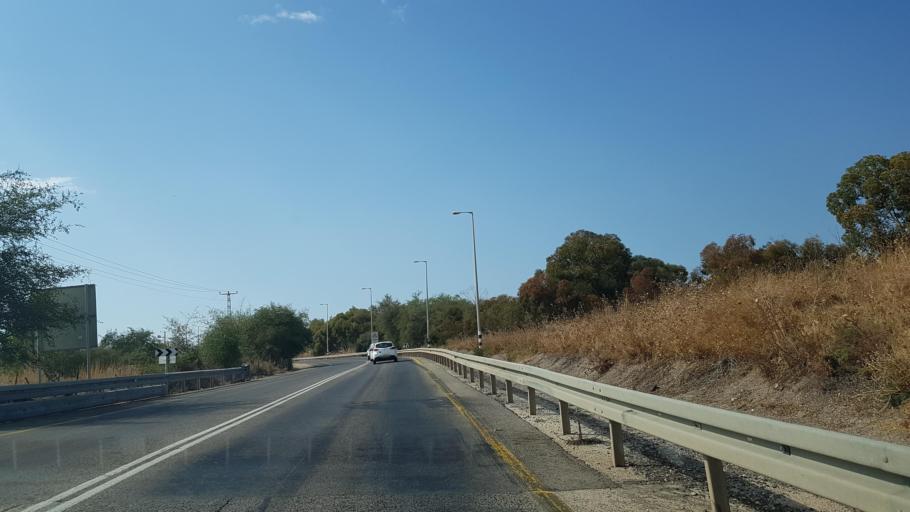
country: SY
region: Quneitra
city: Al Butayhah
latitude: 32.9101
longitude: 35.5818
